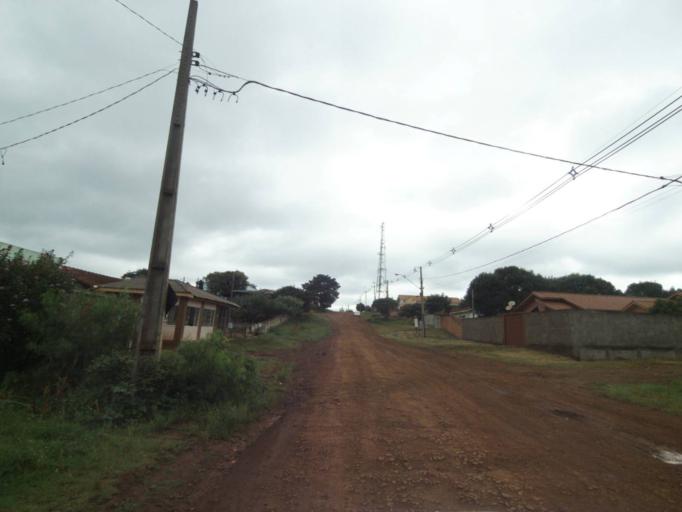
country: BR
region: Parana
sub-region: Pitanga
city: Pitanga
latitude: -24.9406
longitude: -51.8746
